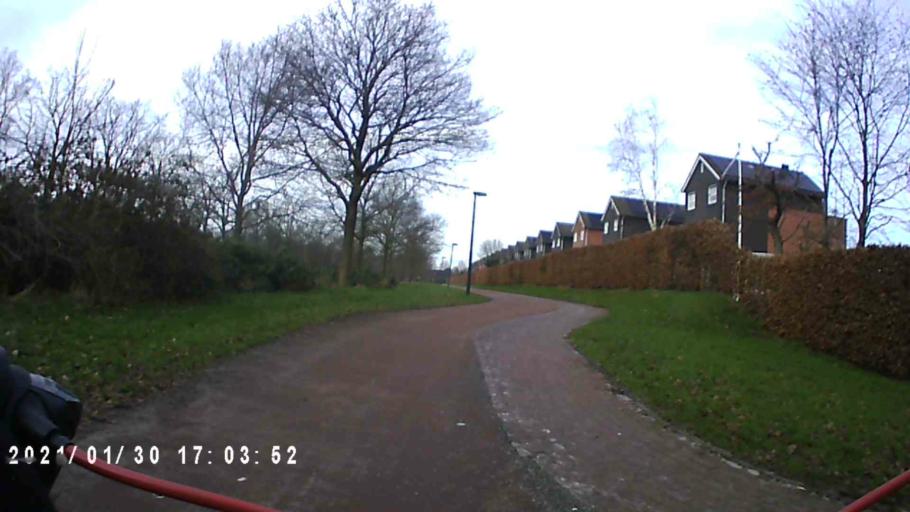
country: NL
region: Groningen
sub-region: Gemeente Leek
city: Leek
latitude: 53.1553
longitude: 6.3704
